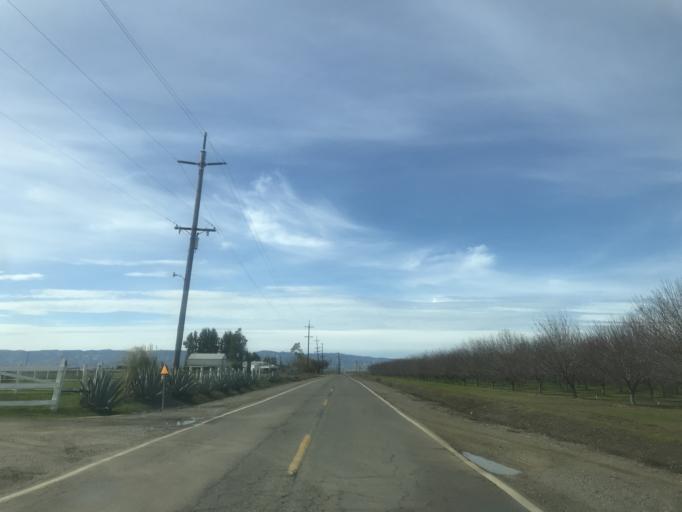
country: US
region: California
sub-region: Yolo County
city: Cottonwood
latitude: 38.6636
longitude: -121.8915
